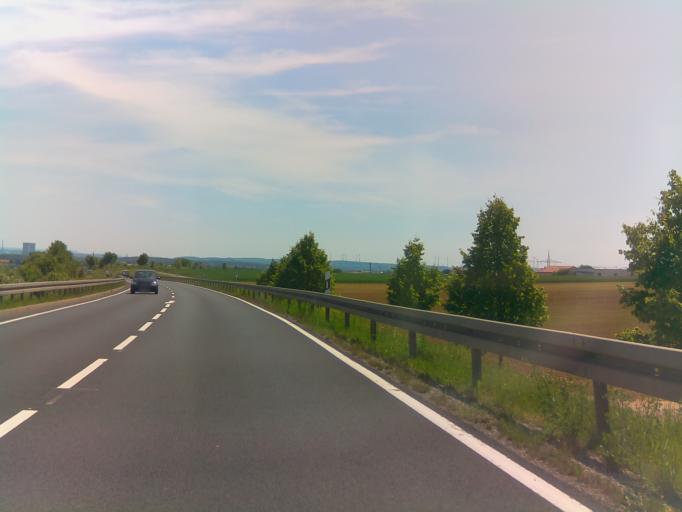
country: DE
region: Bavaria
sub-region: Regierungsbezirk Unterfranken
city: Euerbach
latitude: 50.0705
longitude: 10.1458
